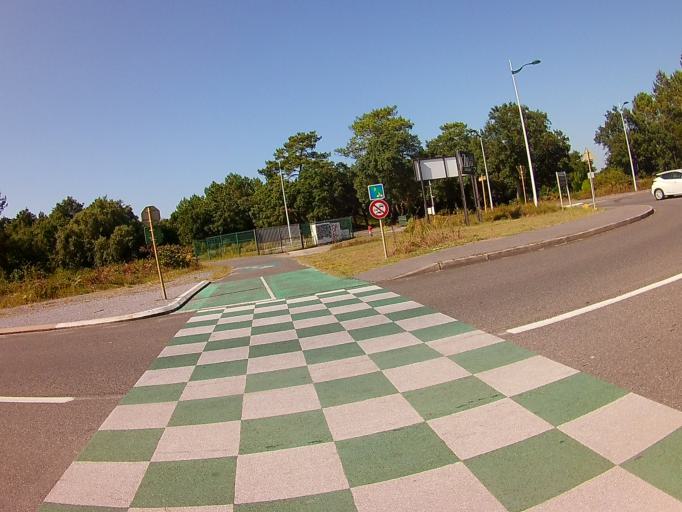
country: FR
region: Aquitaine
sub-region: Departement des Landes
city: Labenne
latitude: 43.5914
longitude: -1.4476
